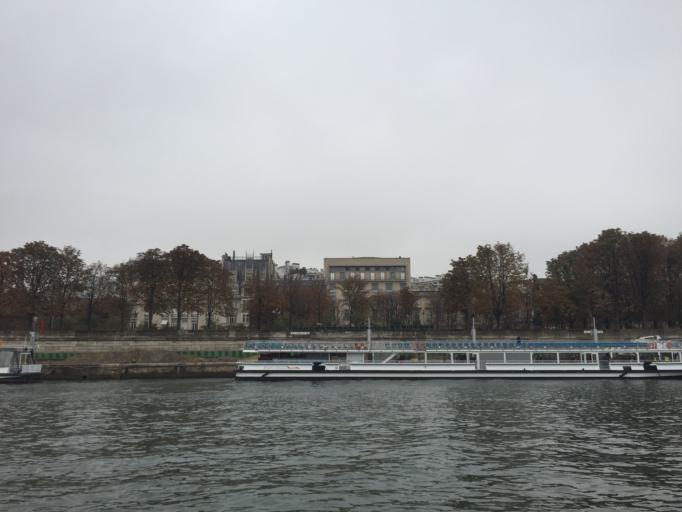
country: FR
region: Ile-de-France
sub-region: Departement des Hauts-de-Seine
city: Levallois-Perret
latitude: 48.8635
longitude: 2.3044
